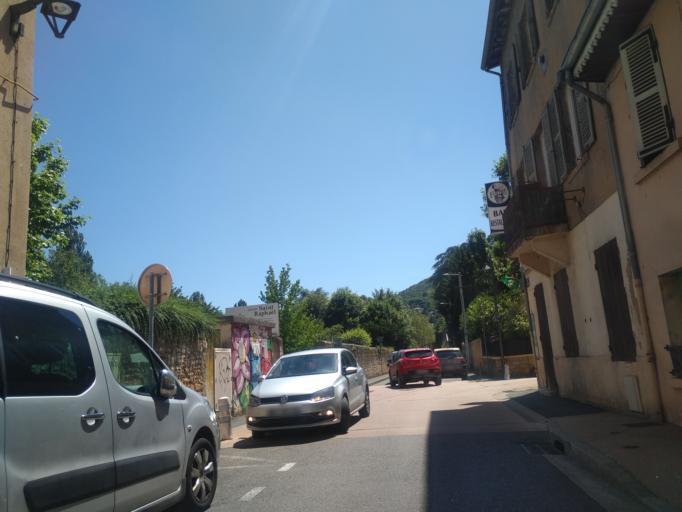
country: FR
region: Rhone-Alpes
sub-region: Departement du Rhone
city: Rochetaillee-sur-Saone
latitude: 45.8438
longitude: 4.8313
